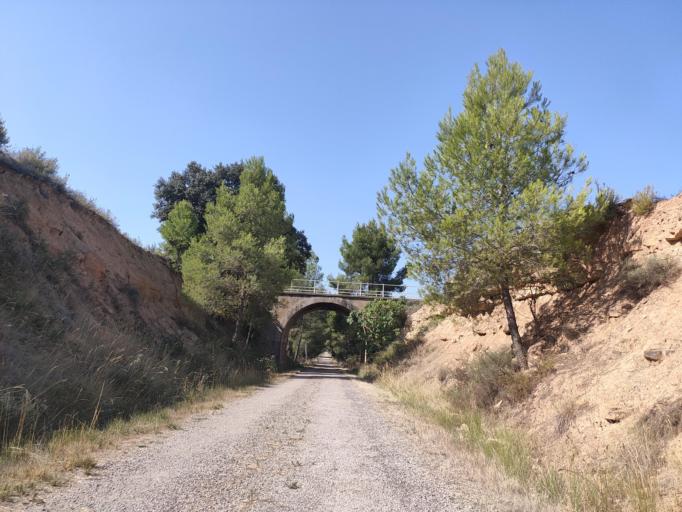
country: ES
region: Catalonia
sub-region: Provincia de Tarragona
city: Horta de Sant Joan
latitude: 40.9635
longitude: 0.3090
